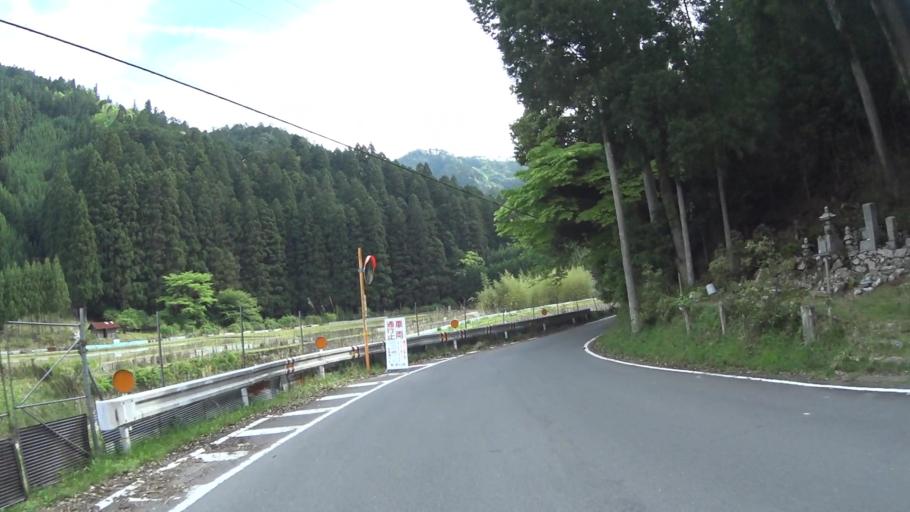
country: JP
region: Kyoto
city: Kameoka
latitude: 35.1227
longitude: 135.6010
